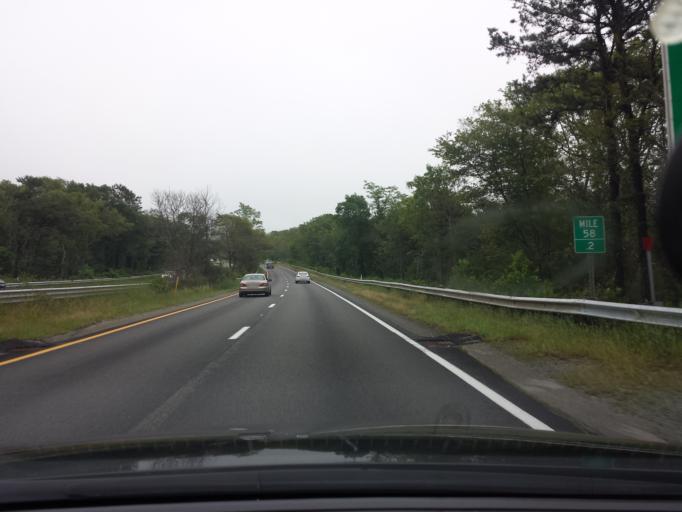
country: US
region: Massachusetts
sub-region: Barnstable County
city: Sandwich
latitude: 41.7418
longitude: -70.5064
